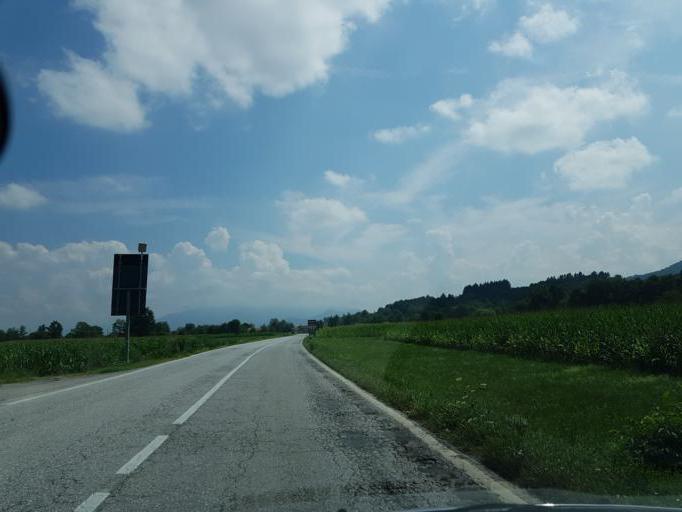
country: IT
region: Piedmont
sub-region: Provincia di Cuneo
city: San Rocco
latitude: 44.3898
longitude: 7.4596
